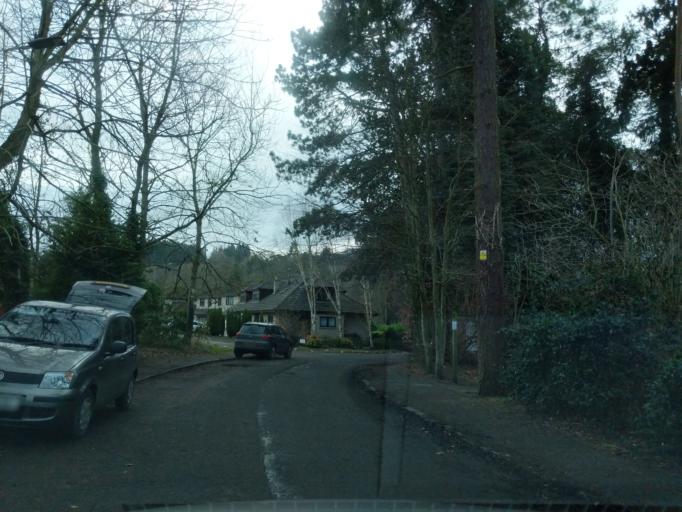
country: GB
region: Scotland
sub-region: South Lanarkshire
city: Carluke
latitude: 55.6975
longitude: -3.8656
